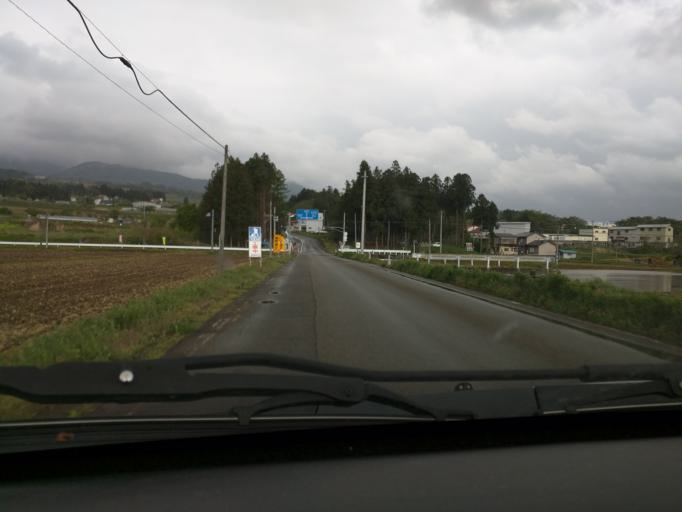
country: JP
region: Fukushima
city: Kitakata
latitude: 37.6401
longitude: 139.9279
